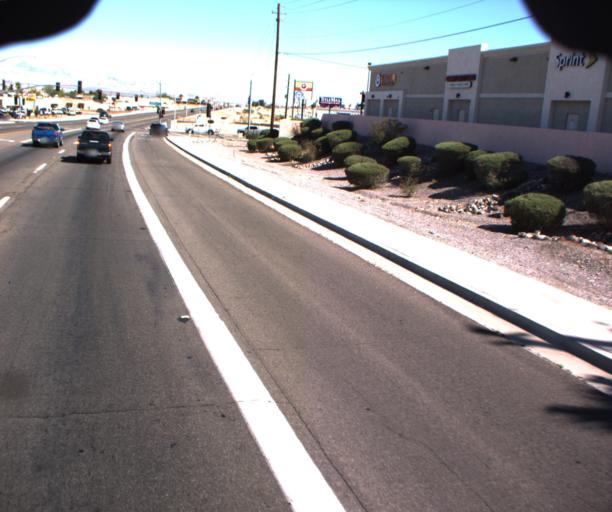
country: US
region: Arizona
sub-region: Mohave County
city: Bullhead City
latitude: 35.0832
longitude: -114.5972
